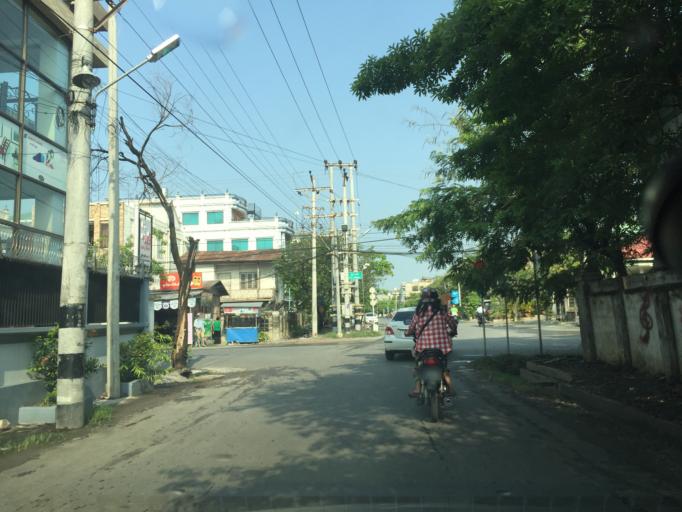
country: MM
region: Mandalay
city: Mandalay
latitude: 21.9731
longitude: 96.0985
